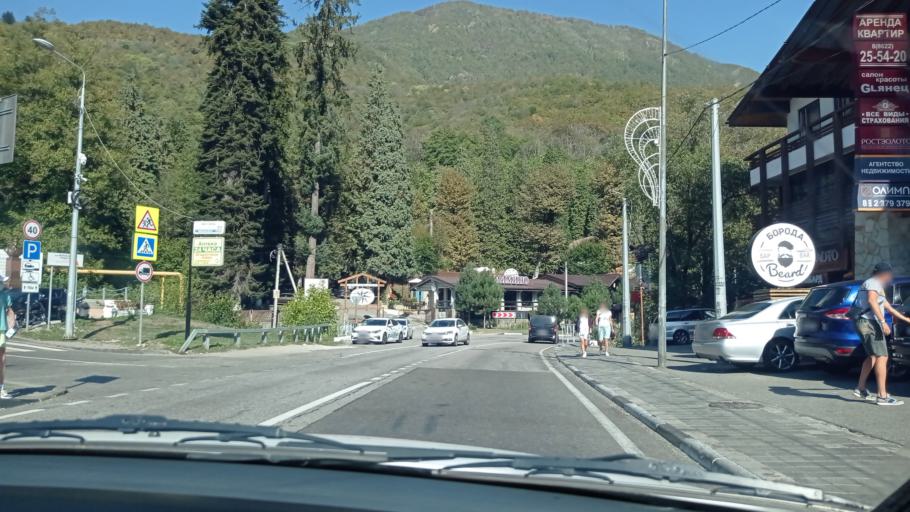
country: RU
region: Krasnodarskiy
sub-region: Sochi City
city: Krasnaya Polyana
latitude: 43.6822
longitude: 40.2127
